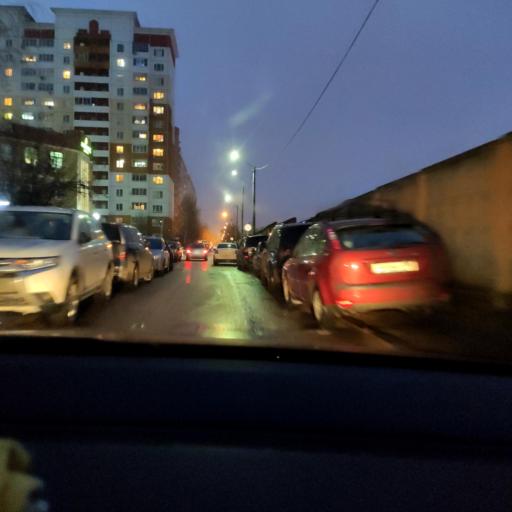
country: RU
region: Moskovskaya
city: Lesnoy Gorodok
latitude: 55.6567
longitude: 37.1994
